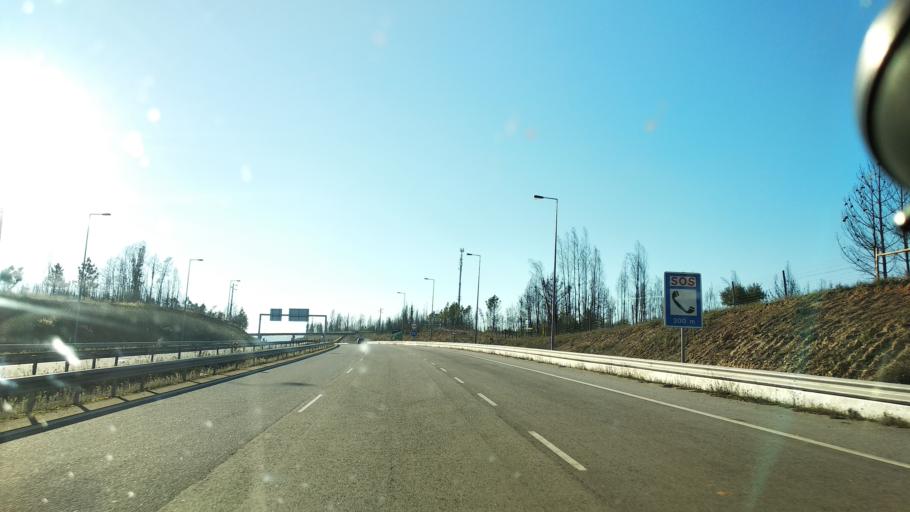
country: PT
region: Santarem
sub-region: Macao
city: Macao
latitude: 39.5296
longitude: -7.9532
